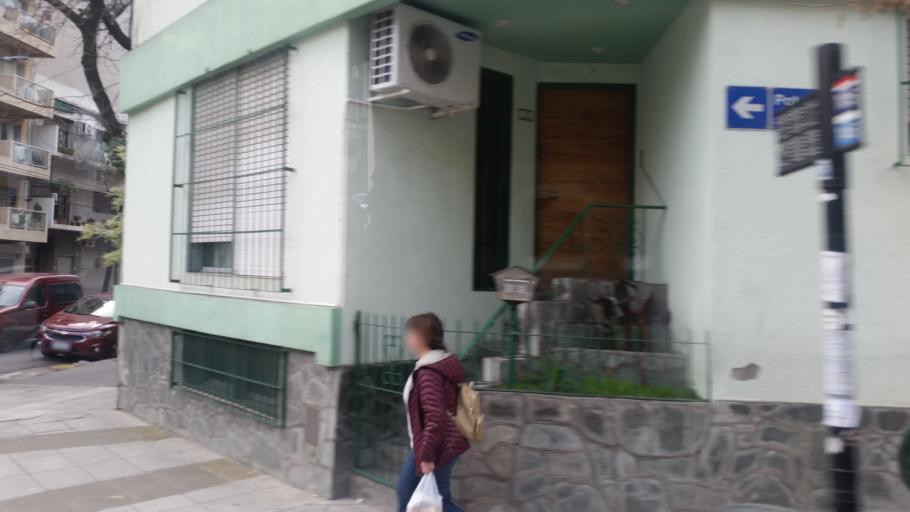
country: AR
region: Buenos Aires F.D.
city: Colegiales
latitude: -34.6072
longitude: -58.4275
